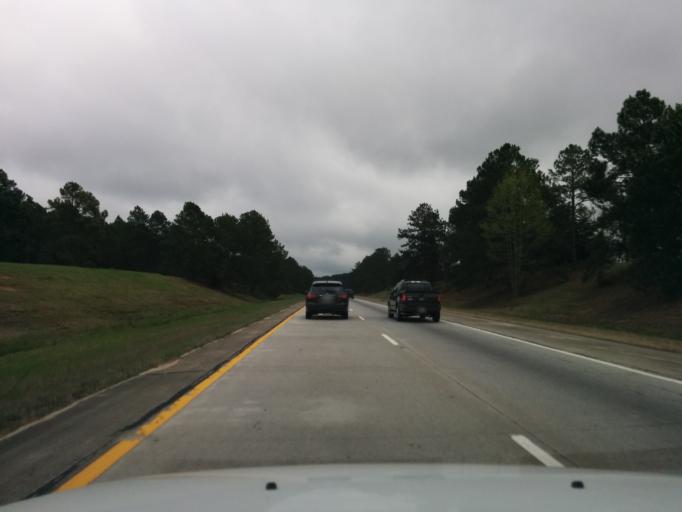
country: US
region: Georgia
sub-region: Candler County
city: Metter
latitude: 32.3786
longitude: -82.2014
